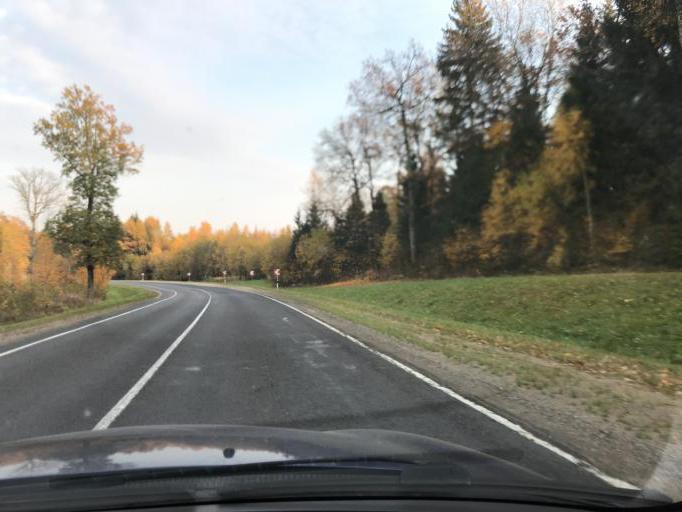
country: BY
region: Grodnenskaya
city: Navahrudak
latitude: 53.5885
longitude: 25.8962
